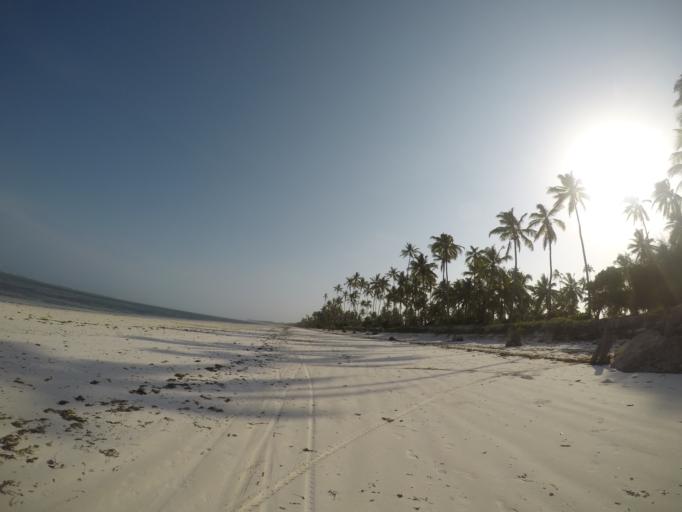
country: TZ
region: Zanzibar Central/South
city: Nganane
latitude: -6.2059
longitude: 39.5349
